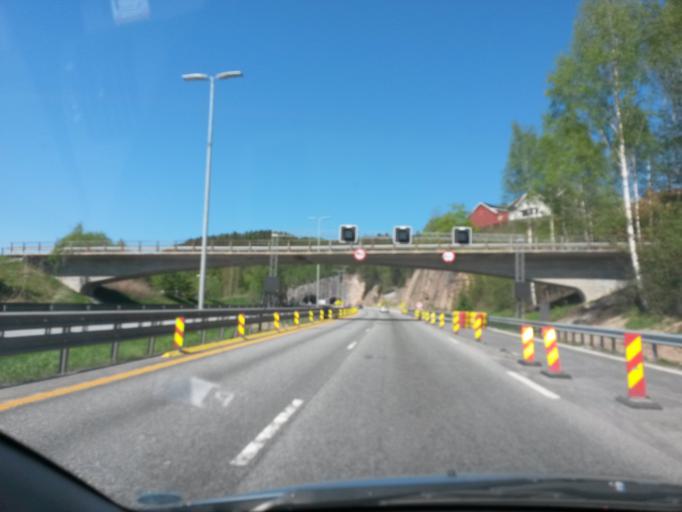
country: NO
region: Buskerud
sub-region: Lier
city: Tranby
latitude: 59.7876
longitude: 10.2731
